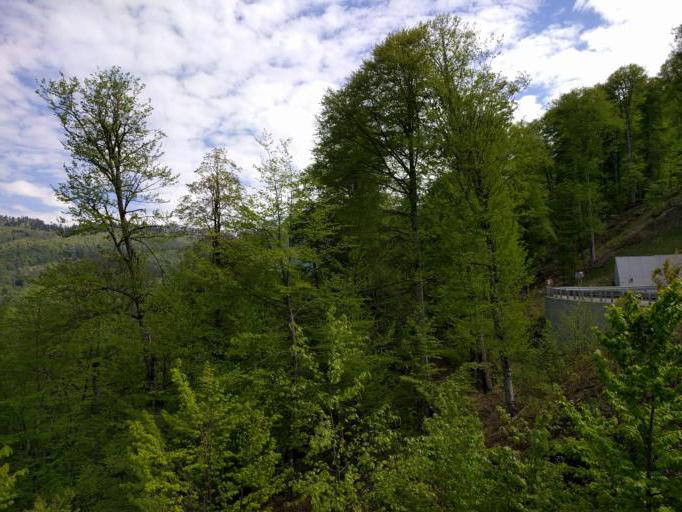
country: RU
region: Krasnodarskiy
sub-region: Sochi City
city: Krasnaya Polyana
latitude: 43.6646
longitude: 40.3095
